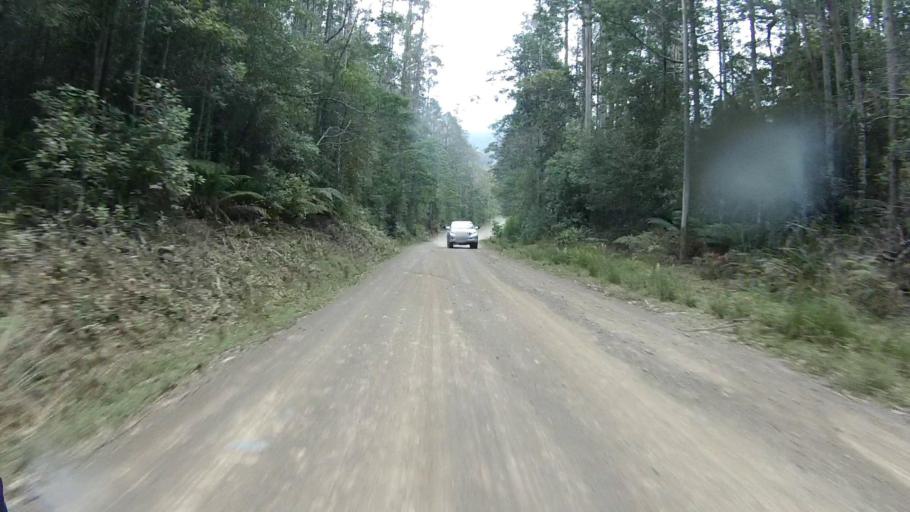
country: AU
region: Tasmania
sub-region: Sorell
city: Sorell
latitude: -42.7085
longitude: 147.8403
